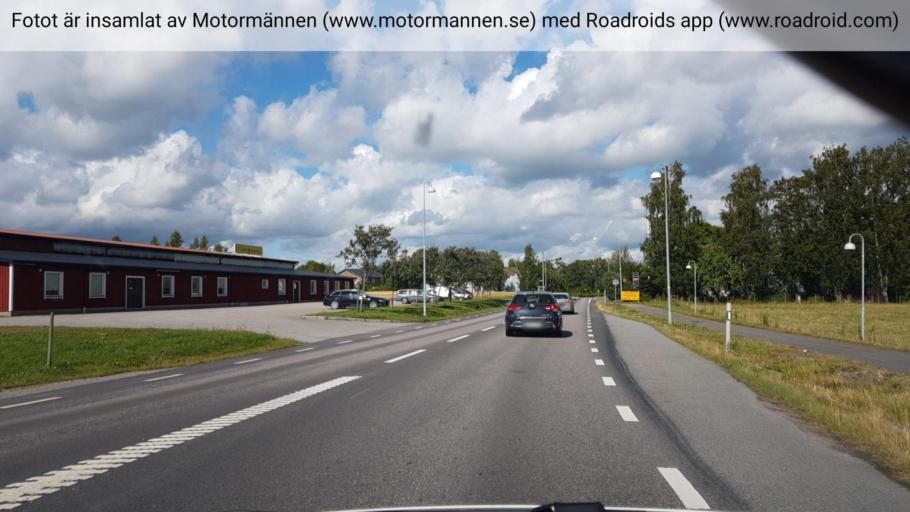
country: SE
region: Vaestra Goetaland
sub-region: Falkopings Kommun
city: Falkoeping
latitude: 57.9823
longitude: 13.5297
